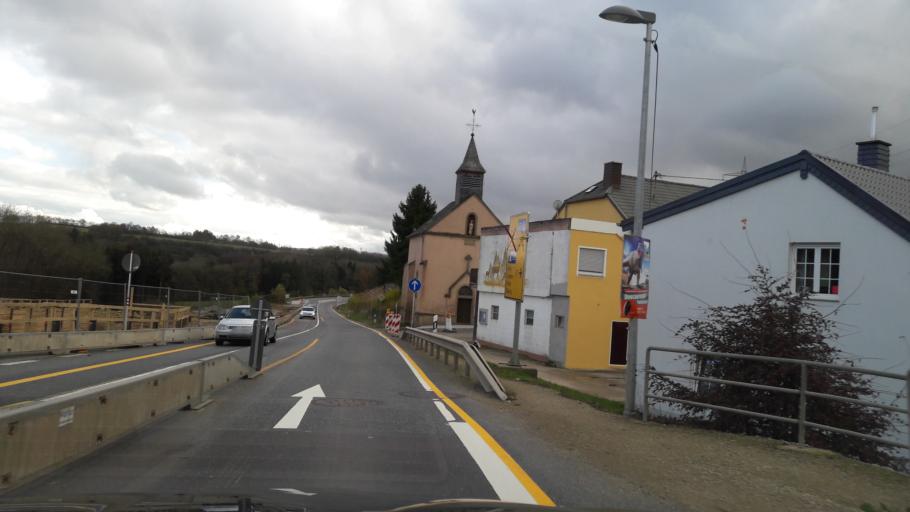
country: DE
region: Rheinland-Pfalz
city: Newel
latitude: 49.7907
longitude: 6.5725
